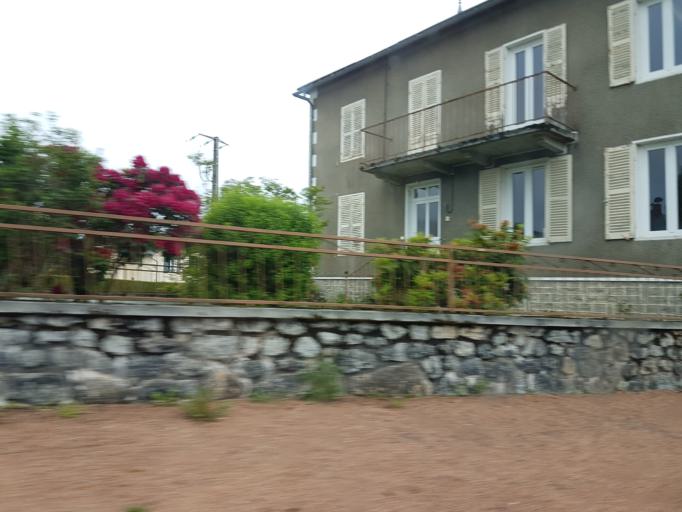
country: FR
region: Bourgogne
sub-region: Departement de la Nievre
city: Chateau-Chinon(Ville)
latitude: 47.0427
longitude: 4.0168
